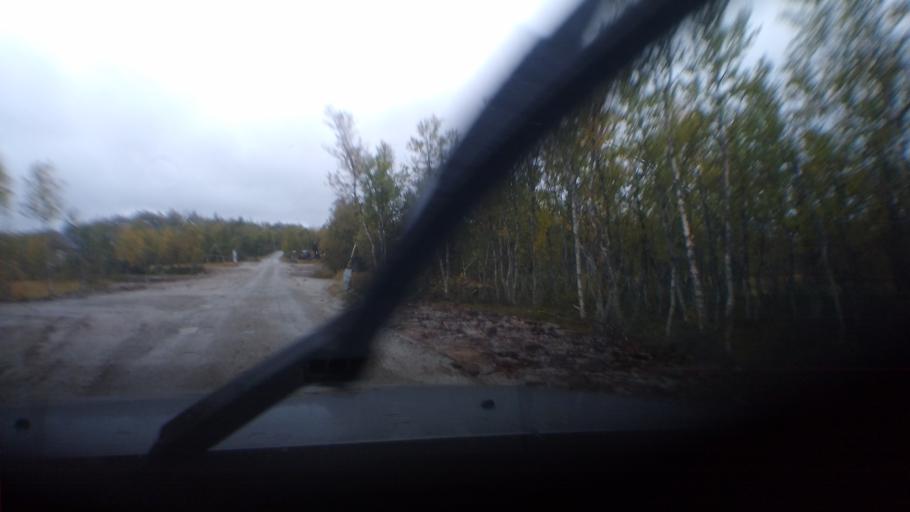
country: NO
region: Oppland
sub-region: Ringebu
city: Ringebu
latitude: 61.6545
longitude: 10.1025
